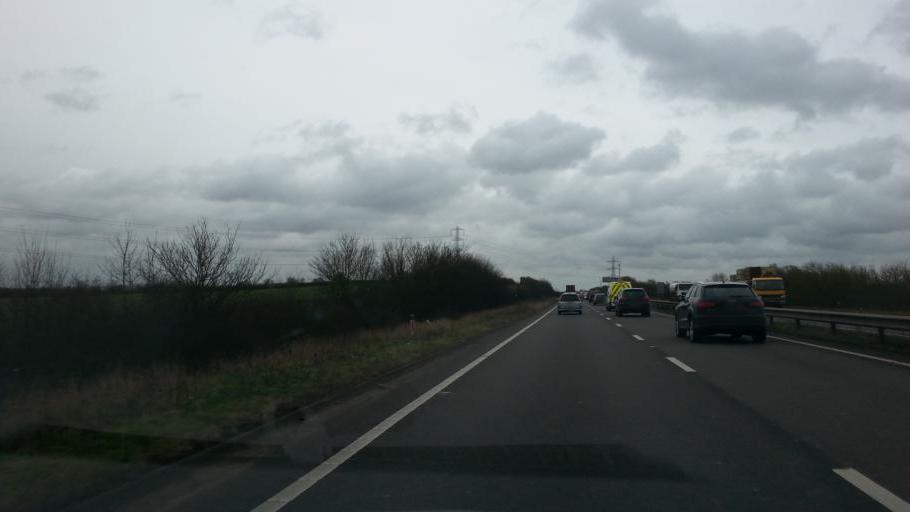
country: GB
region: England
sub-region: Leicestershire
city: Lutterworth
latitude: 52.3954
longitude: -1.1410
